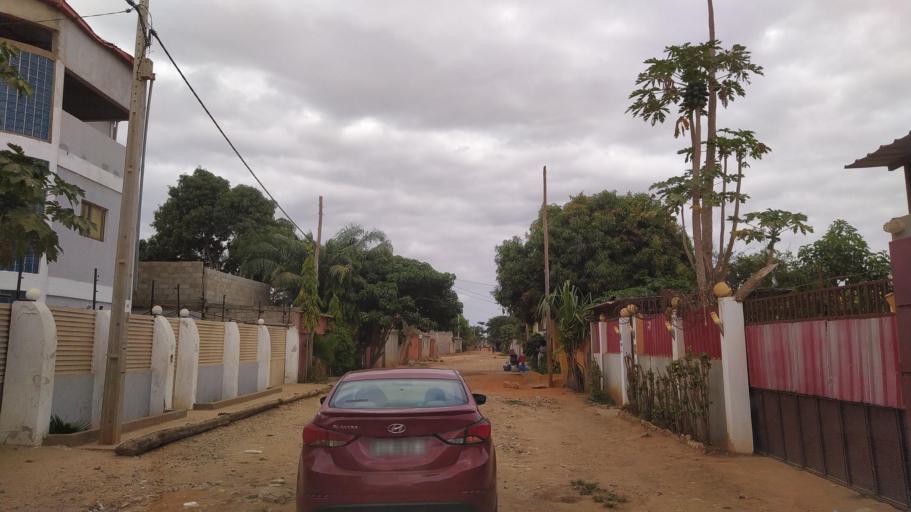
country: AO
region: Luanda
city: Luanda
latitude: -8.9323
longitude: 13.2584
